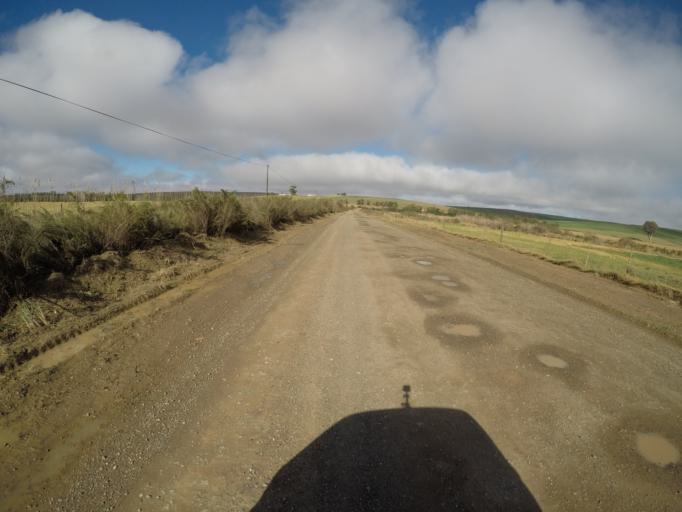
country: ZA
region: Western Cape
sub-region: Cape Winelands District Municipality
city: Ashton
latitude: -34.1243
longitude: 19.8393
